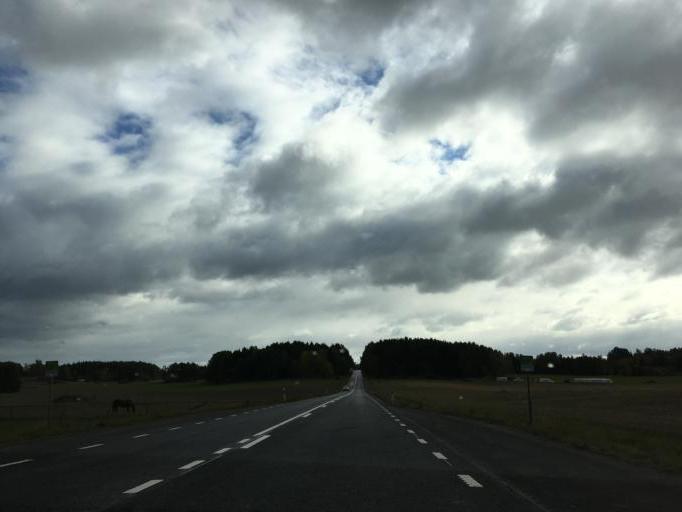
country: SE
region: Soedermanland
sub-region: Nykopings Kommun
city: Olstorp
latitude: 58.8745
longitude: 16.6765
